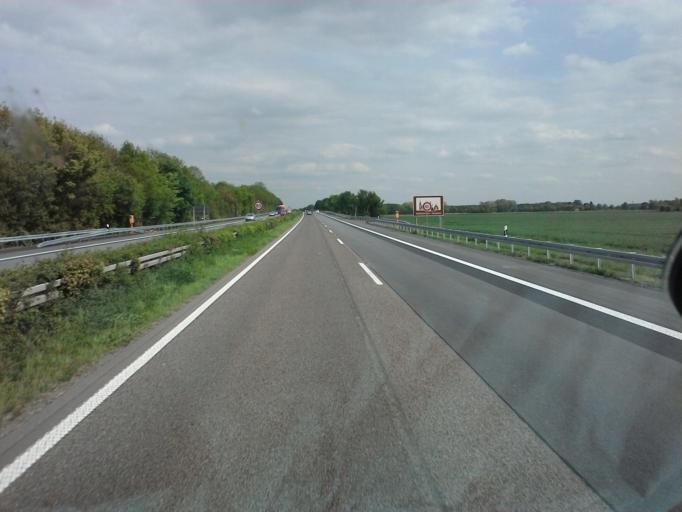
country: DE
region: North Rhine-Westphalia
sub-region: Regierungsbezirk Dusseldorf
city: Goch
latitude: 51.6624
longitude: 6.1473
